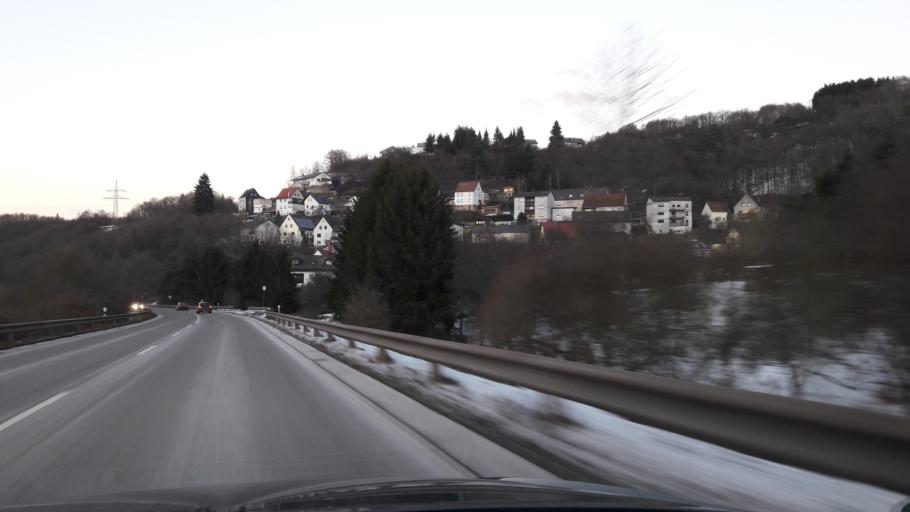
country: DE
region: Rheinland-Pfalz
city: Frauenberg
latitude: 49.6705
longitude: 7.2872
